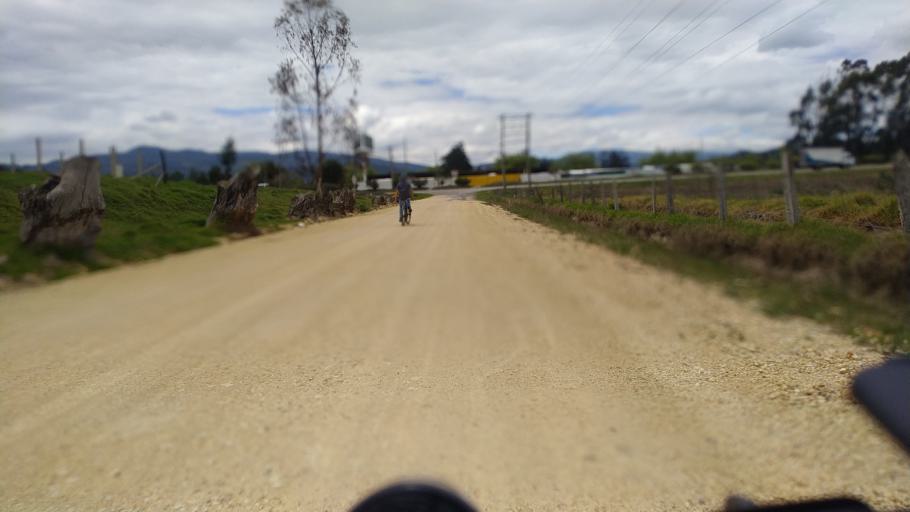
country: CO
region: Boyaca
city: Duitama
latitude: 5.7904
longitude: -73.0691
